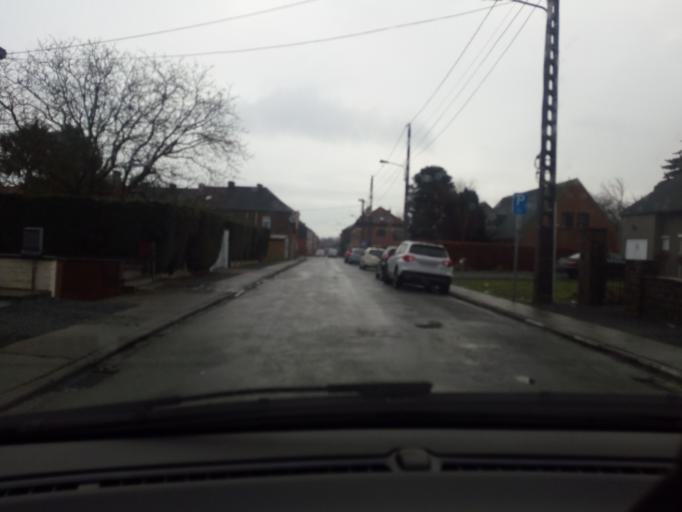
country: BE
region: Wallonia
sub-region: Province du Hainaut
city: Frameries
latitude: 50.4025
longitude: 3.8907
